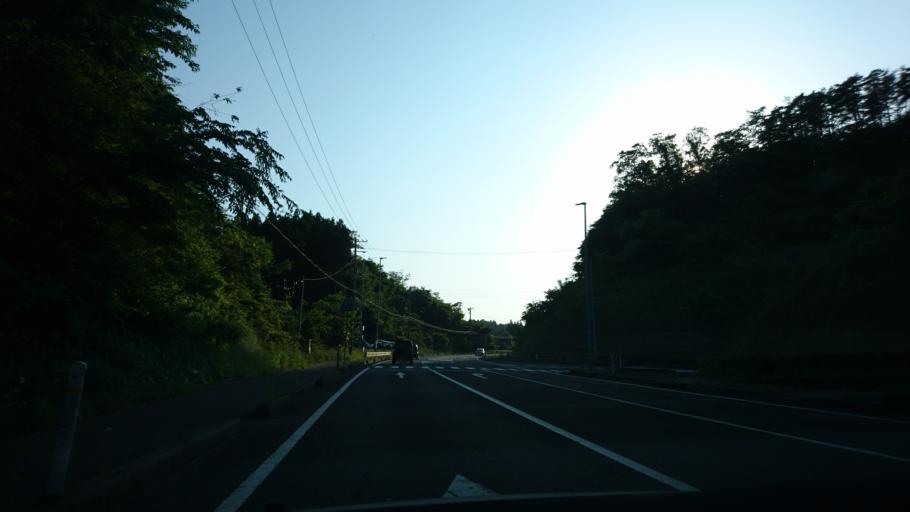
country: JP
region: Iwate
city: Ofunato
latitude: 38.9142
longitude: 141.5125
